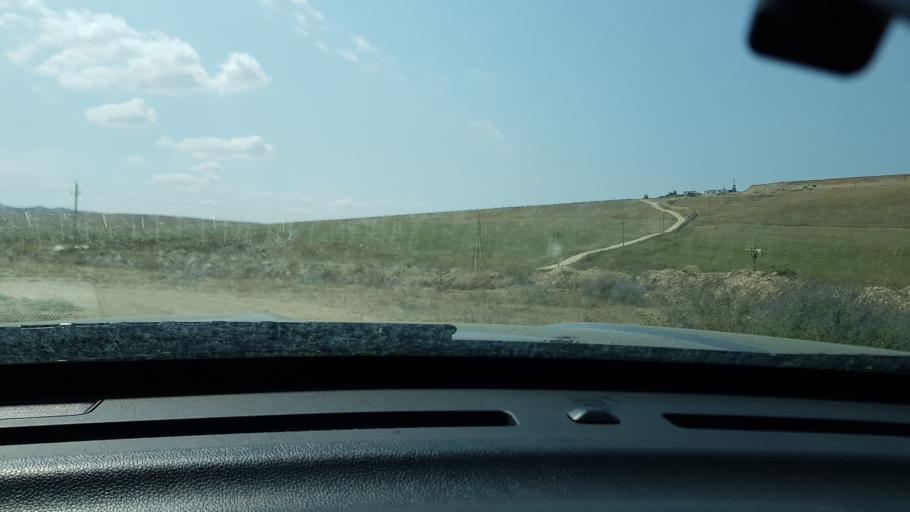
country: TM
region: Ahal
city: Baharly
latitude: 38.3960
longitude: 56.9343
